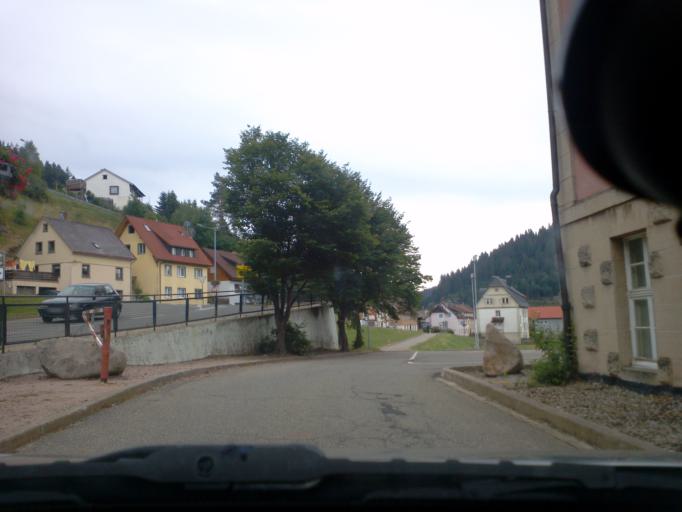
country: DE
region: Baden-Wuerttemberg
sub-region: Freiburg Region
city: Vohrenbach
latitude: 48.0493
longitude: 8.3050
